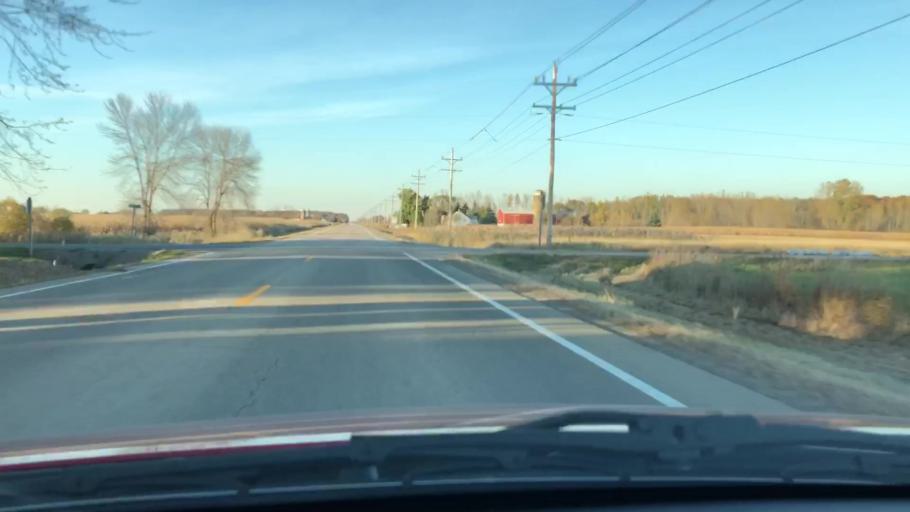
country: US
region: Wisconsin
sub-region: Outagamie County
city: Seymour
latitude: 44.4724
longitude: -88.2910
